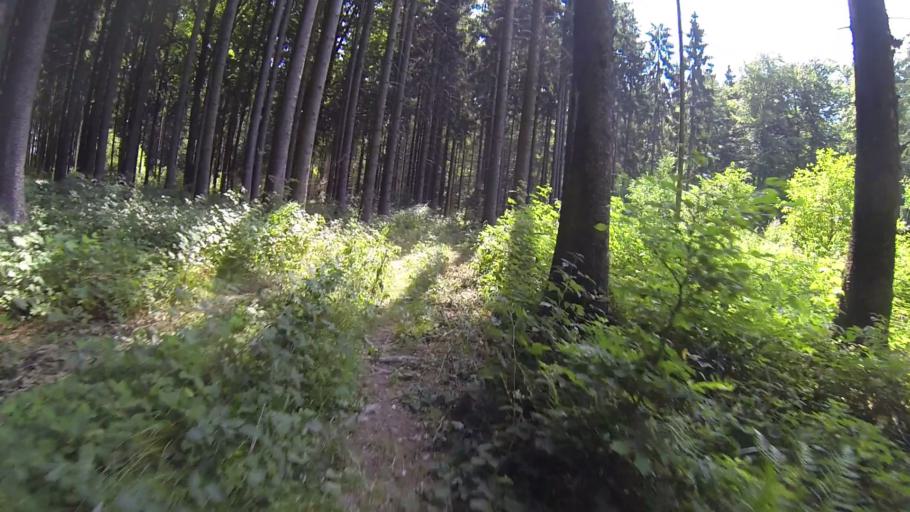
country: DE
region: Baden-Wuerttemberg
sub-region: Regierungsbezirk Stuttgart
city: Herbrechtingen
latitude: 48.6517
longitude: 10.2059
